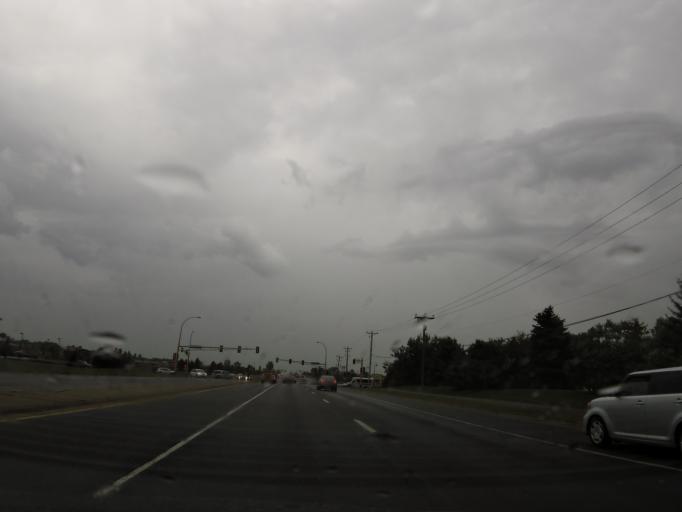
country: US
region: Minnesota
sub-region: Washington County
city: Woodbury
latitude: 44.9406
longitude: -92.9034
